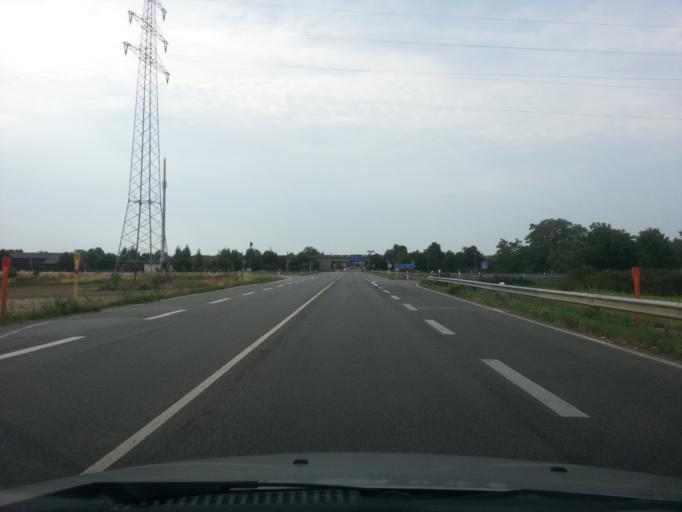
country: DE
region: Rheinland-Pfalz
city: Frankenthal
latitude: 49.5569
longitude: 8.3529
